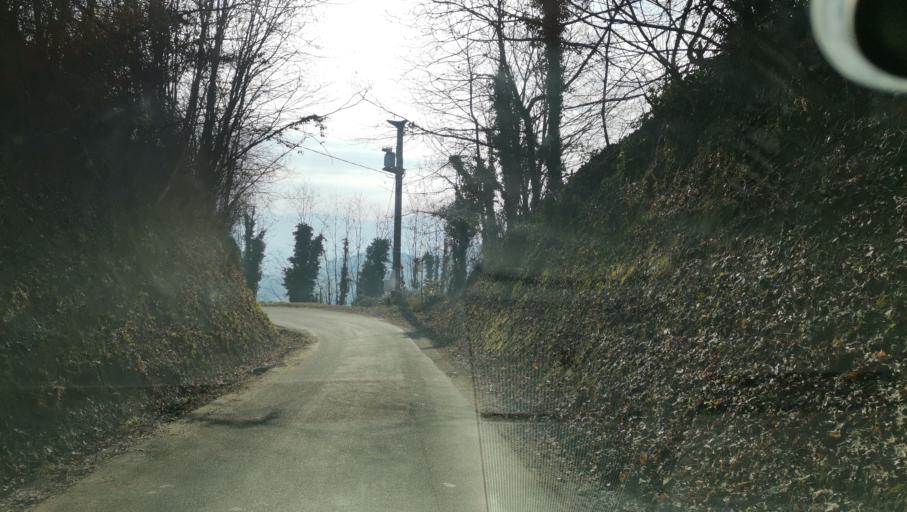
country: IT
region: Piedmont
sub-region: Provincia di Torino
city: Rivalba
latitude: 45.1240
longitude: 7.8929
